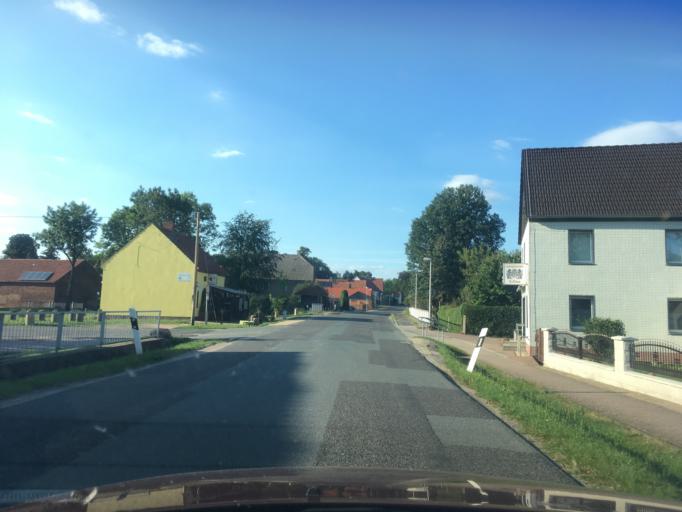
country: PL
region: Lower Silesian Voivodeship
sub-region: Powiat zgorzelecki
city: Piensk
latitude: 51.2360
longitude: 15.0106
